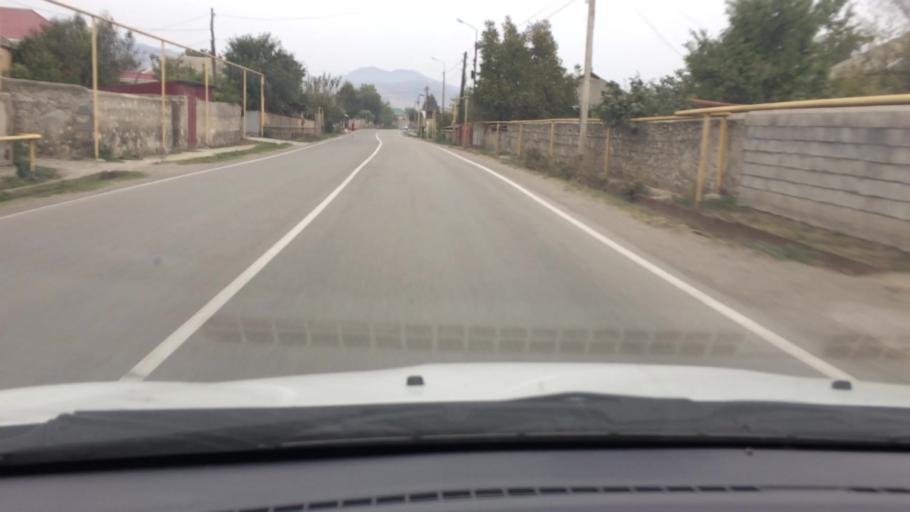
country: AM
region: Tavush
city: Bagratashen
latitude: 41.2403
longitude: 44.8010
